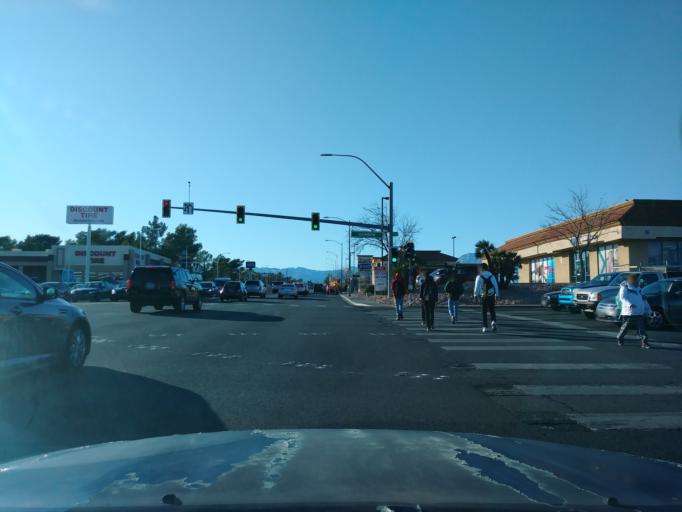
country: US
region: Nevada
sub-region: Clark County
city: Spring Valley
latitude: 36.1592
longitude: -115.2436
